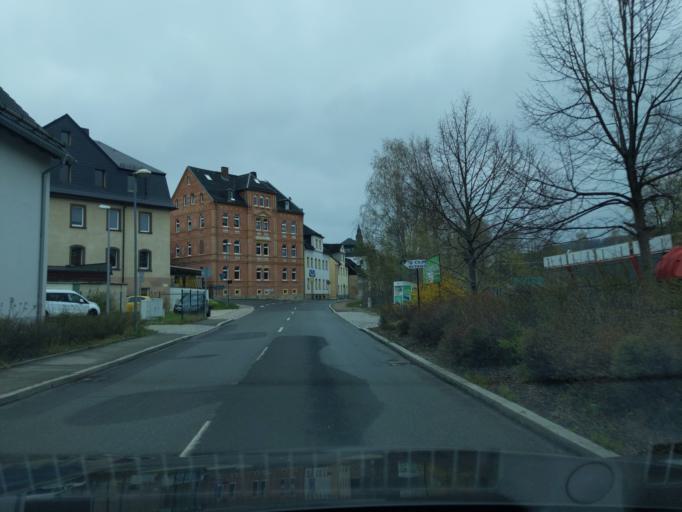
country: DE
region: Saxony
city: Schneeberg
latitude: 50.5881
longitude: 12.6363
